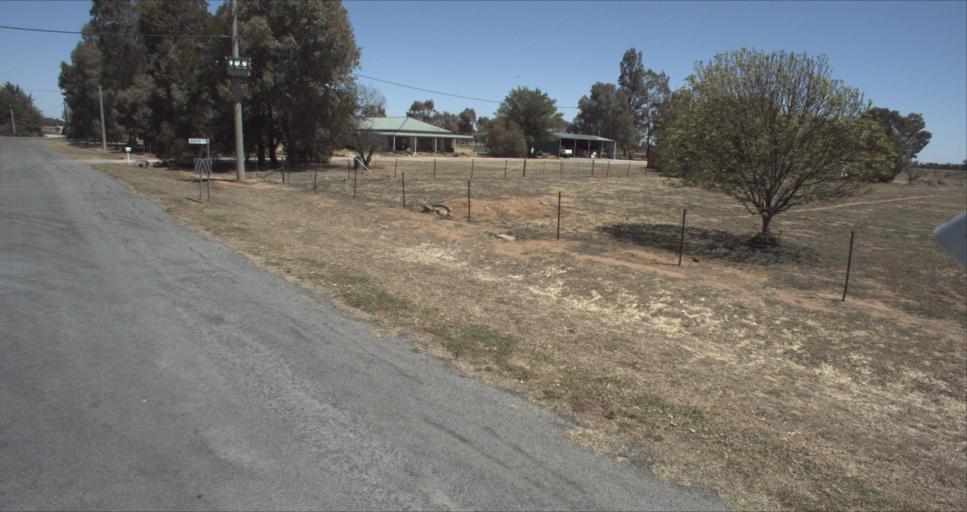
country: AU
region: New South Wales
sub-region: Leeton
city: Leeton
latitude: -34.5203
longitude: 146.4039
